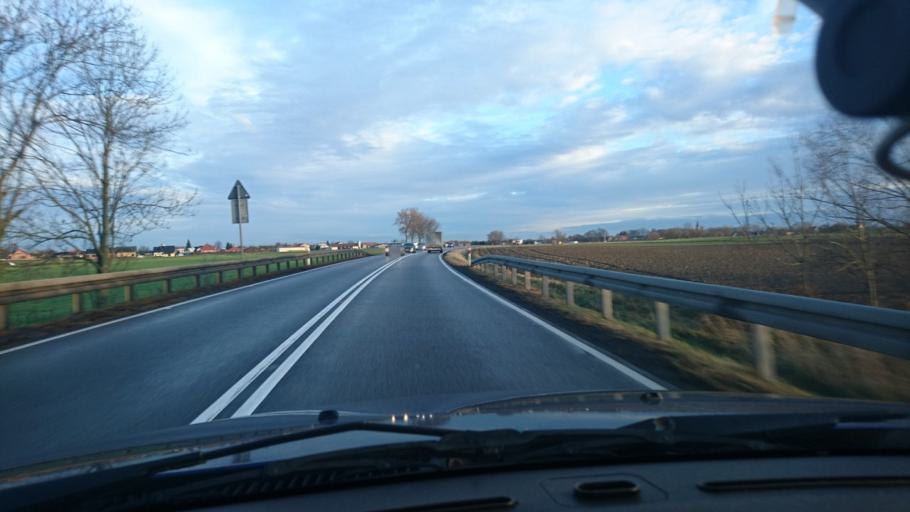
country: PL
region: Greater Poland Voivodeship
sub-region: Powiat kepinski
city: Opatow
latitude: 51.2210
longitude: 18.1323
